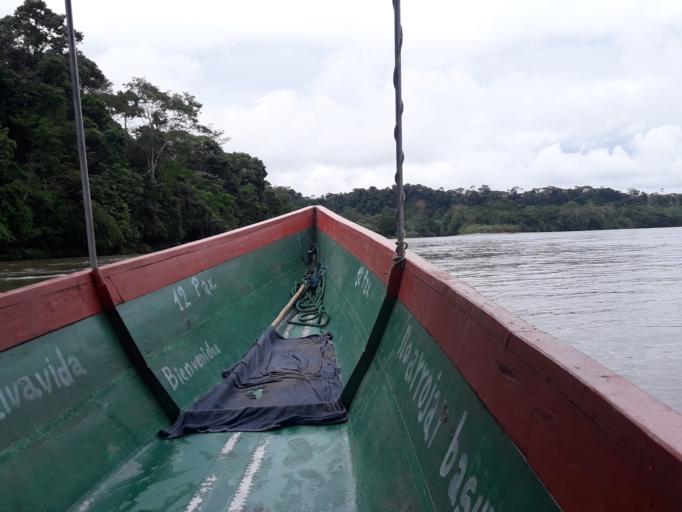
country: EC
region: Napo
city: Tena
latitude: -1.0358
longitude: -77.6617
